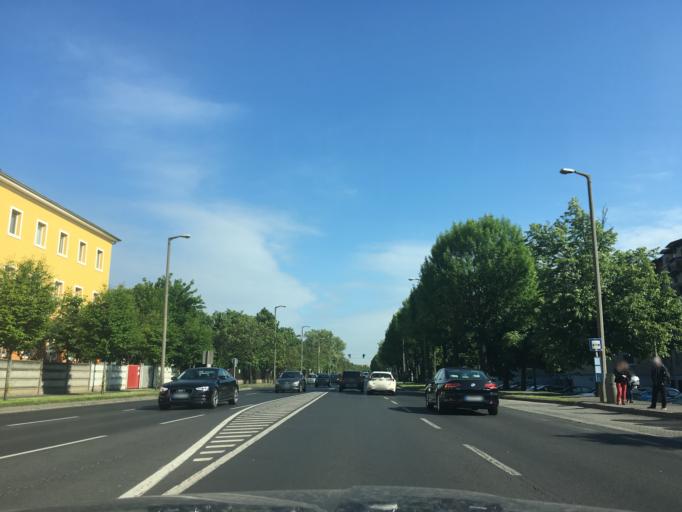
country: HU
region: Hajdu-Bihar
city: Debrecen
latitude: 47.5360
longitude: 21.6119
